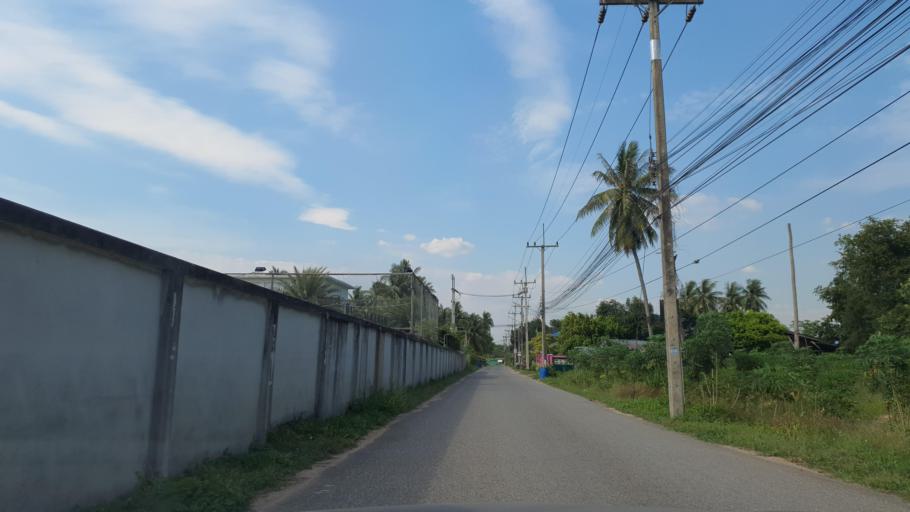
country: TH
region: Chon Buri
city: Sattahip
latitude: 12.7848
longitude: 100.9428
